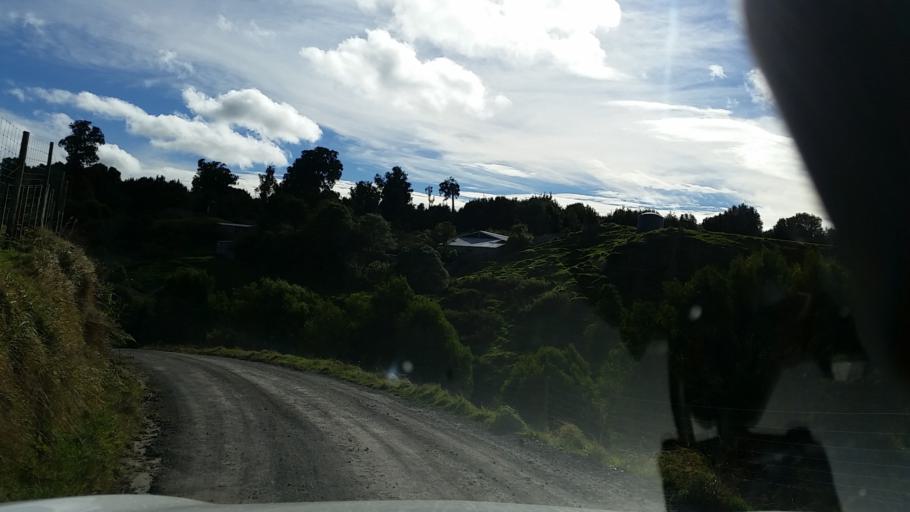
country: NZ
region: Bay of Plenty
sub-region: Rotorua District
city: Rotorua
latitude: -38.0939
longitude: 176.1038
